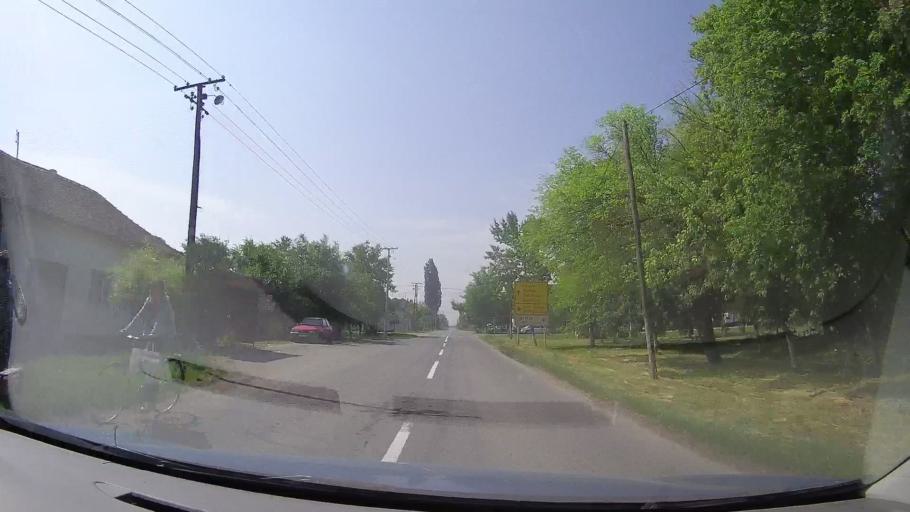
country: RS
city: Jarkovac
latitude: 45.2706
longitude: 20.7645
